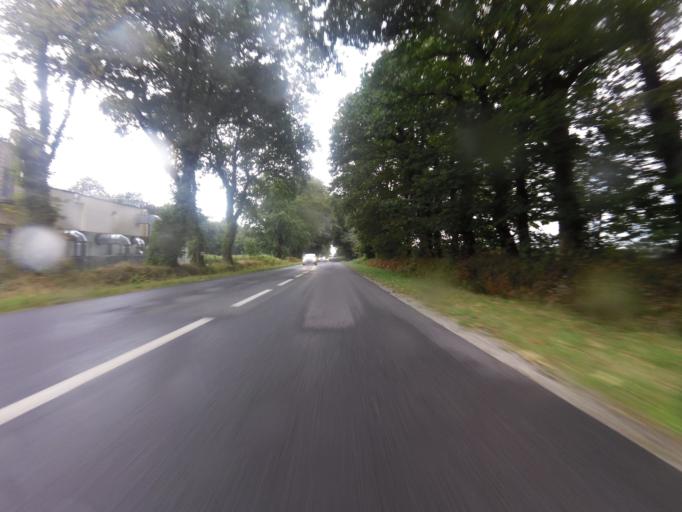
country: FR
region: Brittany
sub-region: Departement du Morbihan
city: Saint-Nolff
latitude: 47.6953
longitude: -2.6416
